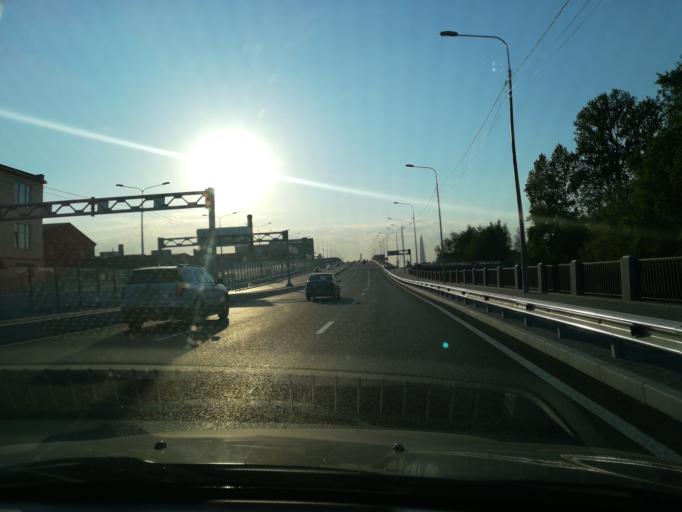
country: RU
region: St.-Petersburg
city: Vasyl'evsky Ostrov
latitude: 59.9545
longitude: 30.2652
